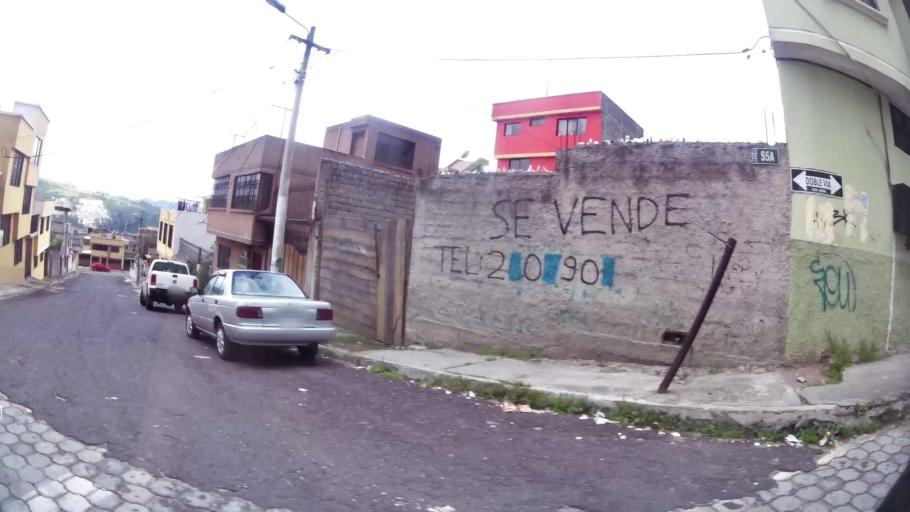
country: EC
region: Pichincha
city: Quito
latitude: -0.2421
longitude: -78.4949
